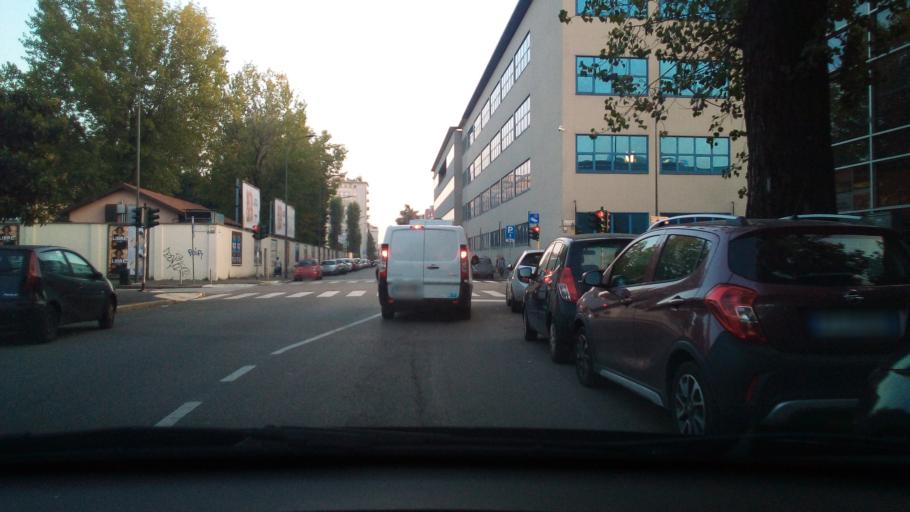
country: IT
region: Lombardy
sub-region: Citta metropolitana di Milano
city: Sesto San Giovanni
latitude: 45.5006
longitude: 9.2287
